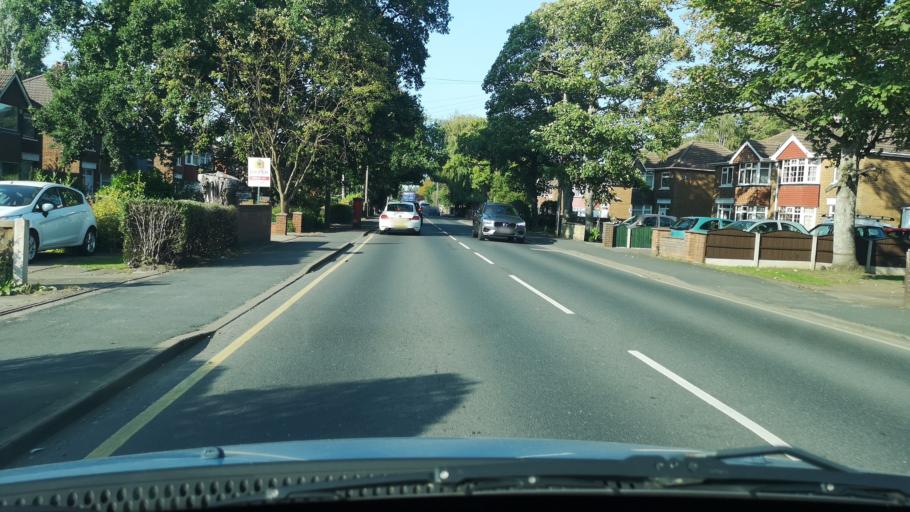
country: GB
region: England
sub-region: North Lincolnshire
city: Scunthorpe
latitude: 53.5870
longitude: -0.6841
